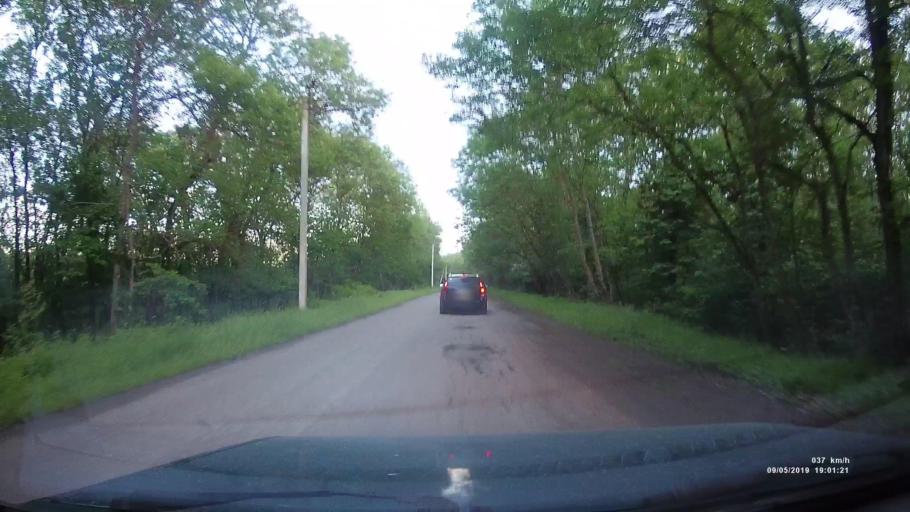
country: RU
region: Krasnodarskiy
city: Kanelovskaya
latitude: 46.7486
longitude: 39.1428
